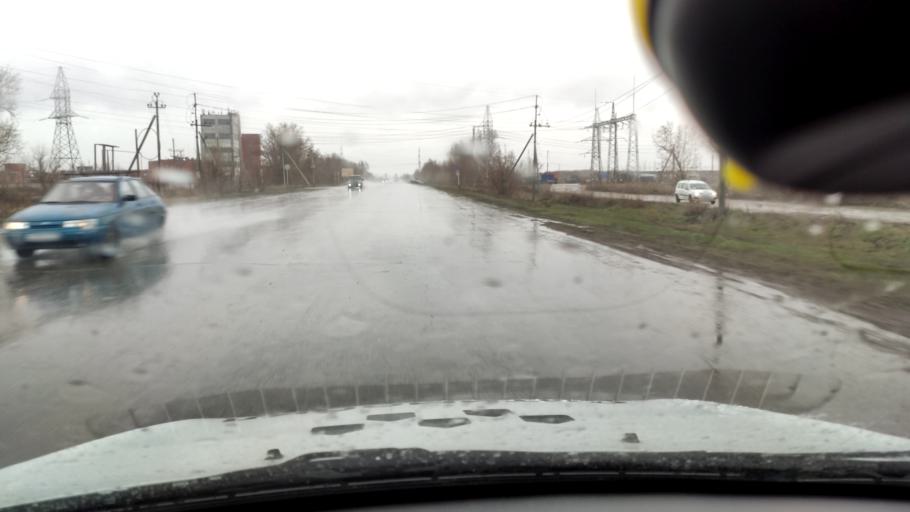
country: RU
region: Samara
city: Tol'yatti
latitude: 53.5877
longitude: 49.4054
